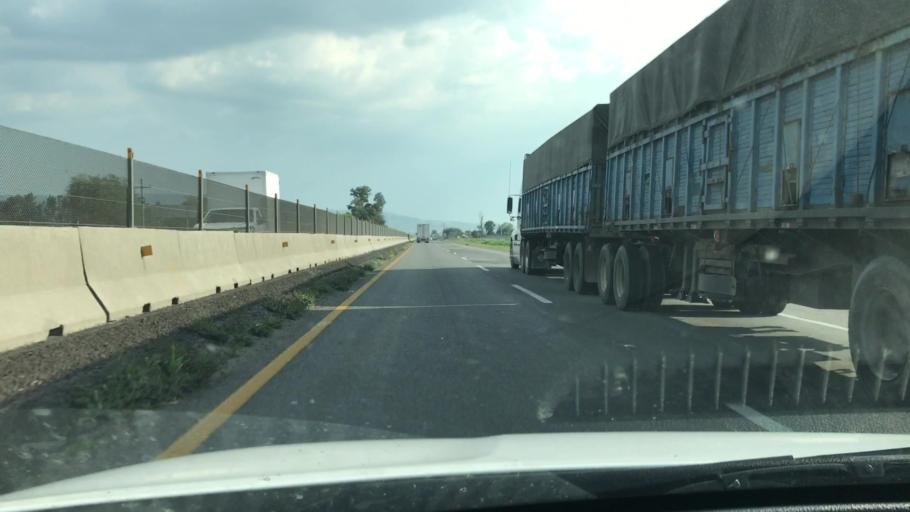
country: MX
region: Guanajuato
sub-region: Abasolo
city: San Bernardo Pena Blanca
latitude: 20.4971
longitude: -101.4822
